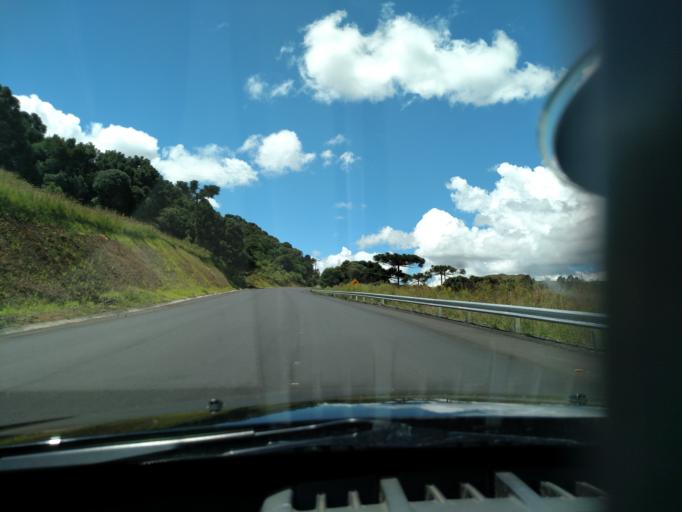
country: BR
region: Santa Catarina
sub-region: Sao Joaquim
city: Sao Joaquim
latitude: -28.2460
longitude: -49.9702
